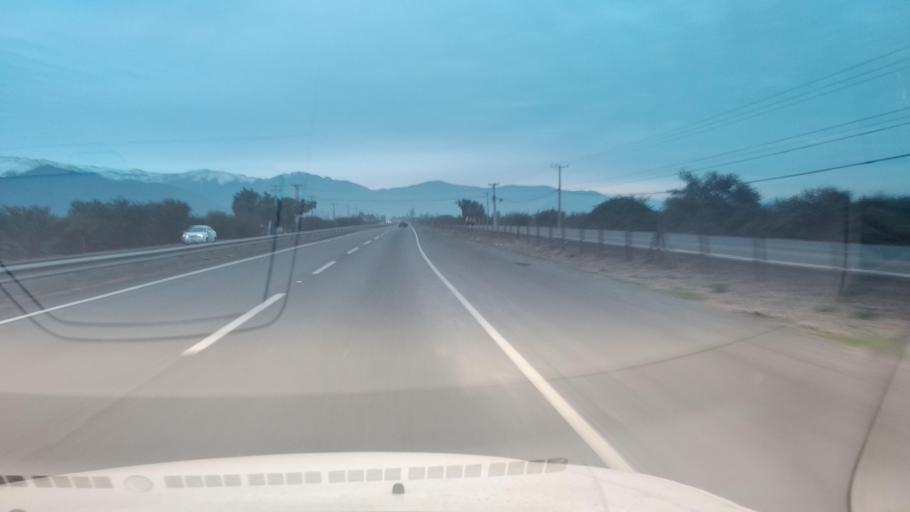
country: CL
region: Santiago Metropolitan
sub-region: Provincia de Chacabuco
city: Chicureo Abajo
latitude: -33.1476
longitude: -70.6569
